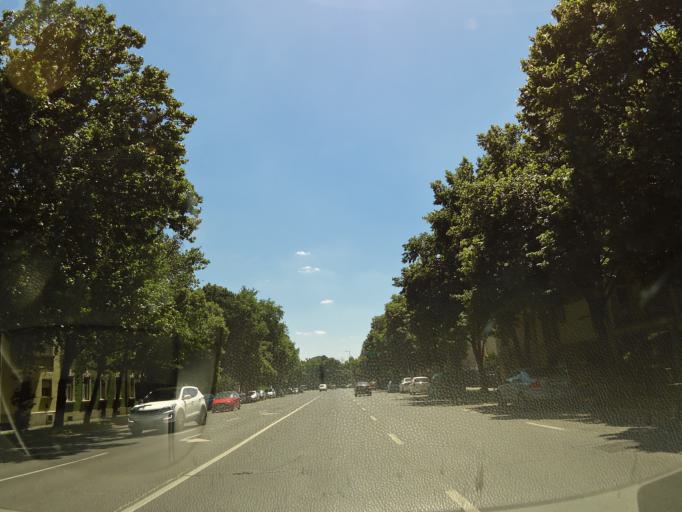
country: HU
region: Csongrad
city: Szeged
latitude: 46.2489
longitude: 20.1379
